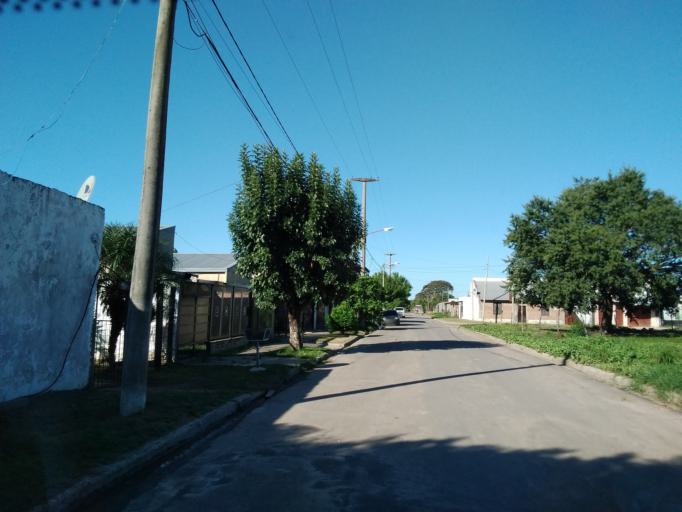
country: AR
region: Corrientes
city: Corrientes
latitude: -27.4588
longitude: -58.7696
